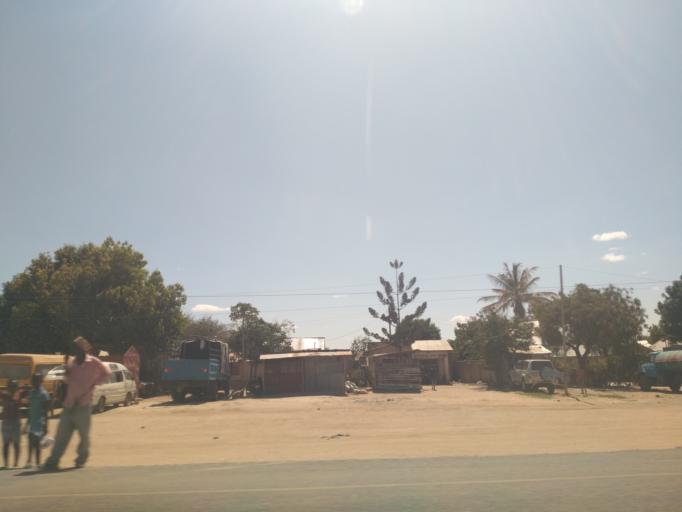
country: TZ
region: Dodoma
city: Dodoma
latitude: -6.1583
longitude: 35.7466
